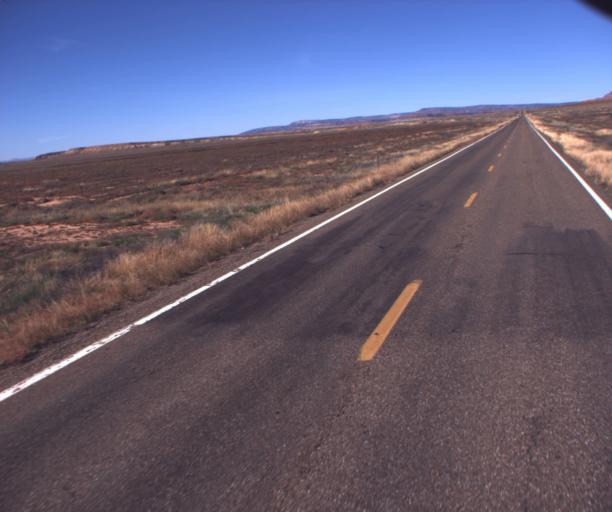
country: US
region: Arizona
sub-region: Coconino County
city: Fredonia
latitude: 36.9250
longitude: -112.4629
